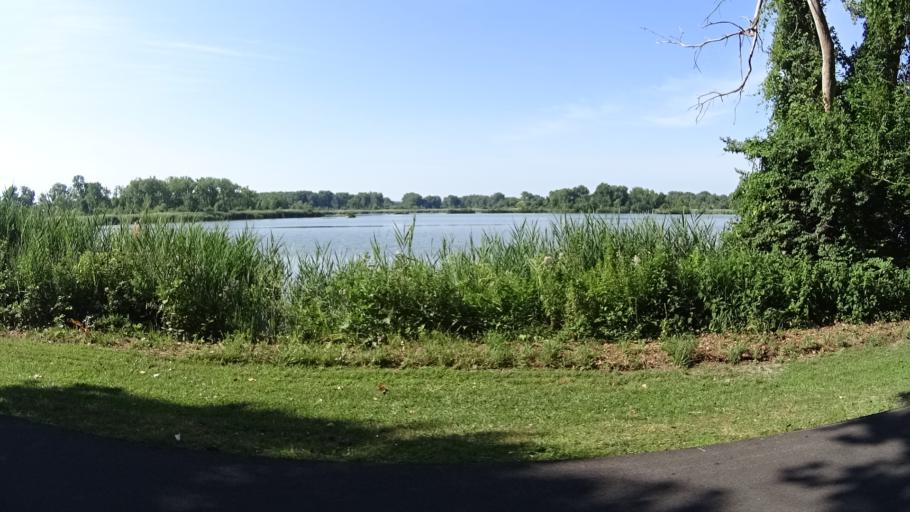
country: US
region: Ohio
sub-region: Erie County
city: Sandusky
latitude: 41.4172
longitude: -82.8308
